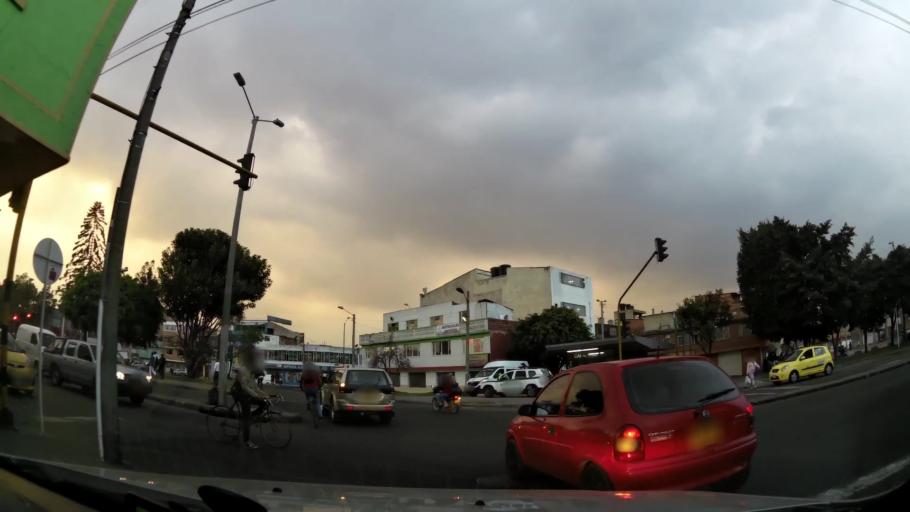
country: CO
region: Bogota D.C.
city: Bogota
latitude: 4.5898
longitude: -74.1384
